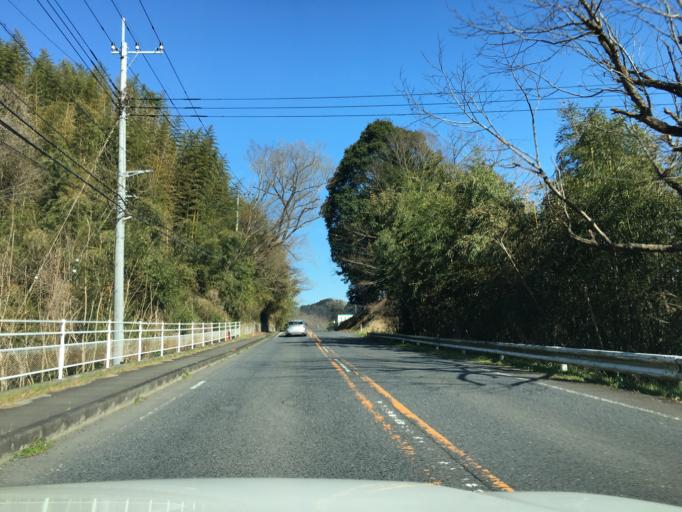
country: JP
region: Tochigi
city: Motegi
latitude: 36.5658
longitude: 140.2763
